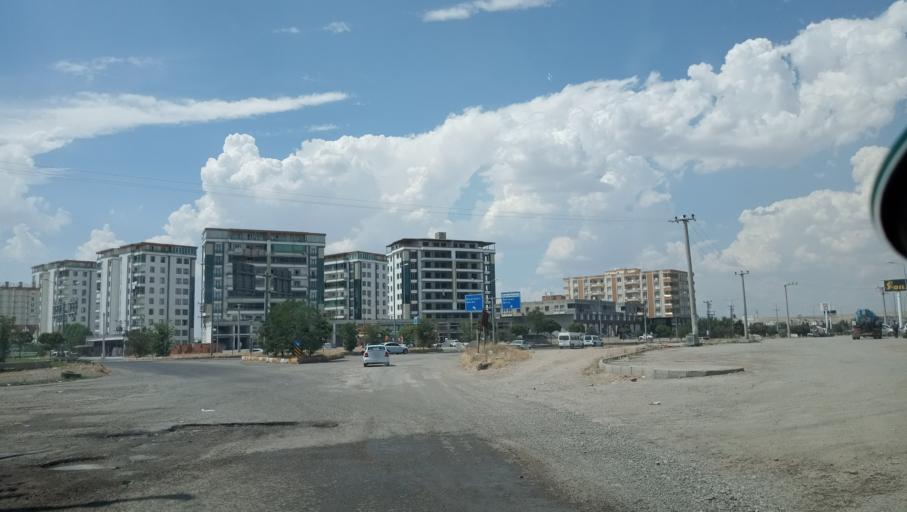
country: TR
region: Diyarbakir
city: Bismil
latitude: 37.8330
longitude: 40.6576
